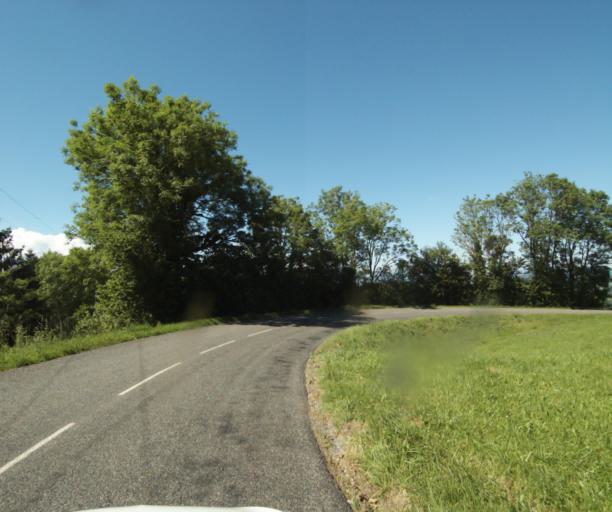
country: FR
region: Rhone-Alpes
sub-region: Departement de la Haute-Savoie
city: Bons-en-Chablais
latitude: 46.2519
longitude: 6.3669
